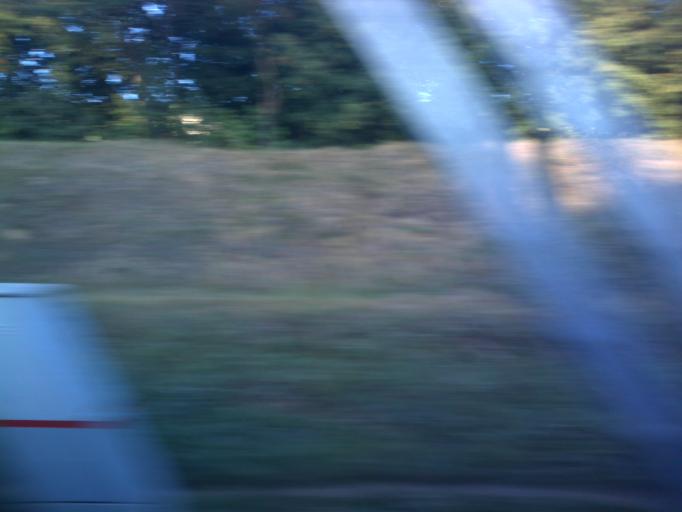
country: RU
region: Moscow
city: Kotlovka
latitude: 55.6776
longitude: 37.6219
